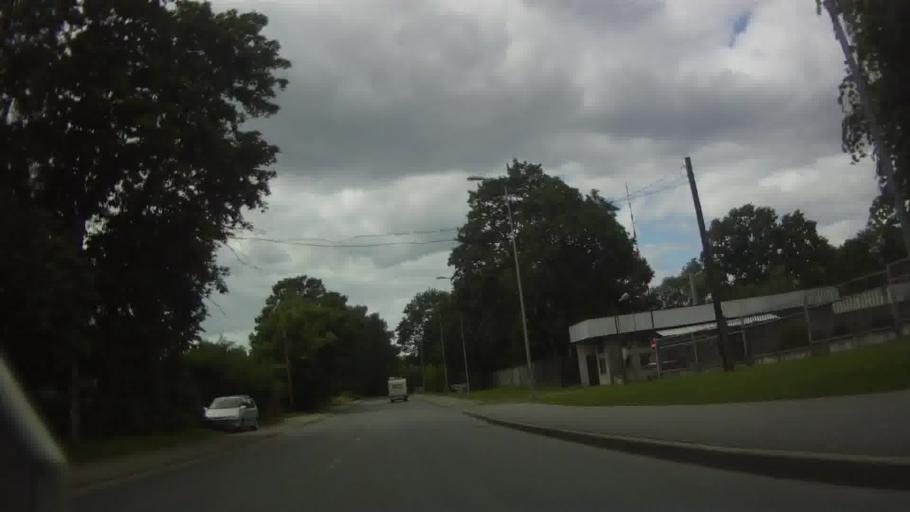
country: LV
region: Kekava
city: Balozi
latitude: 56.9116
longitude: 24.1446
